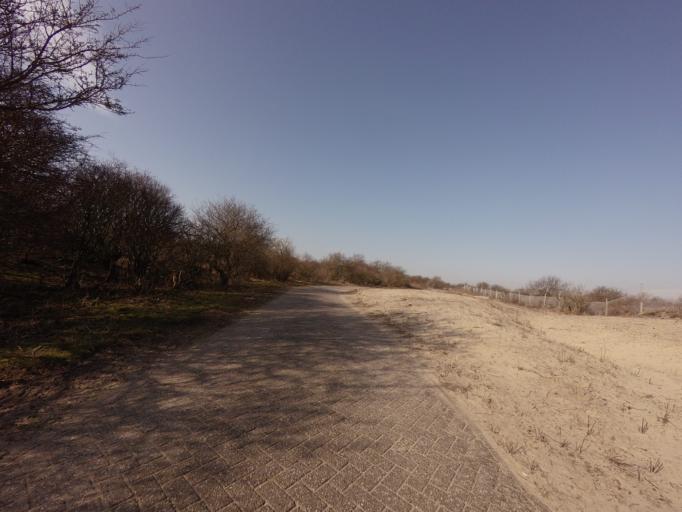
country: NL
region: North Holland
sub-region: Gemeente Zandvoort
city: Zandvoort
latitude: 52.3757
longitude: 4.5696
